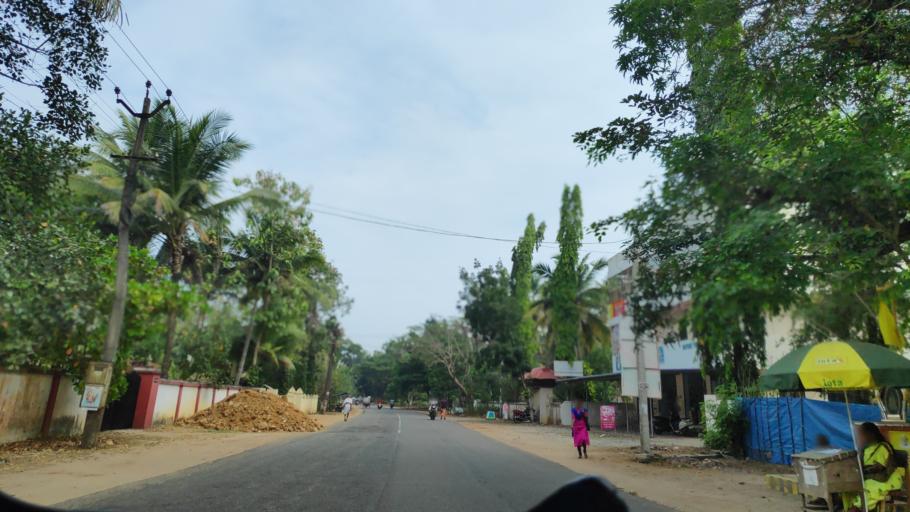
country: IN
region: Kerala
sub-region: Kottayam
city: Vaikam
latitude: 9.7402
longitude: 76.3628
